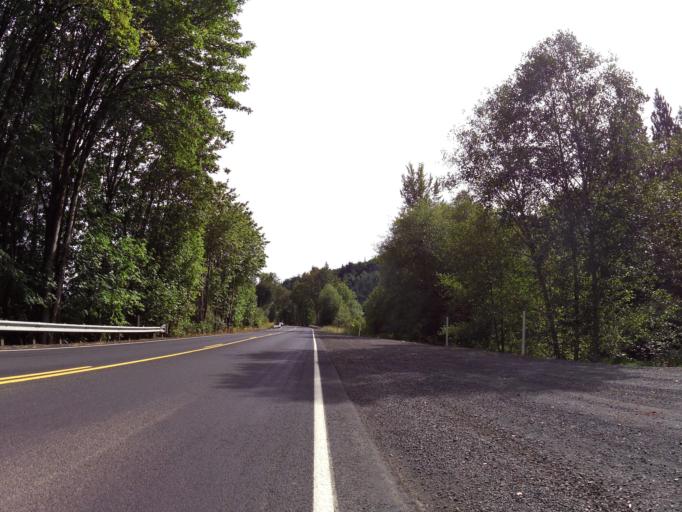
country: US
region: Washington
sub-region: Cowlitz County
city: Castle Rock
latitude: 46.3389
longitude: -122.9370
